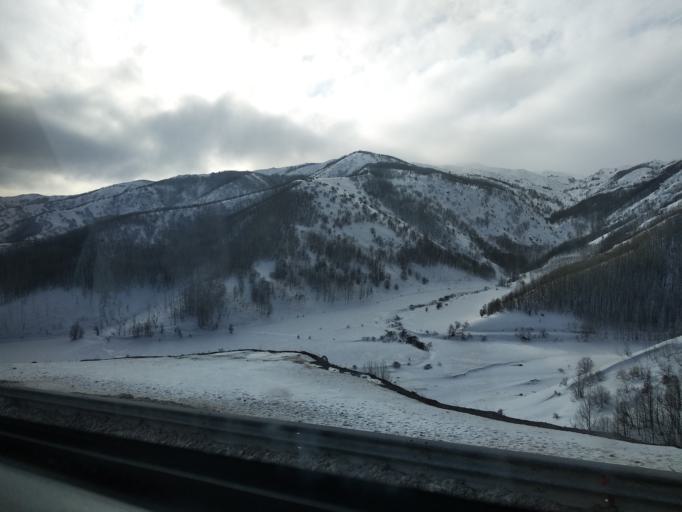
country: TR
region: Erzincan
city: Catalarmut
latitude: 39.8992
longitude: 39.3946
